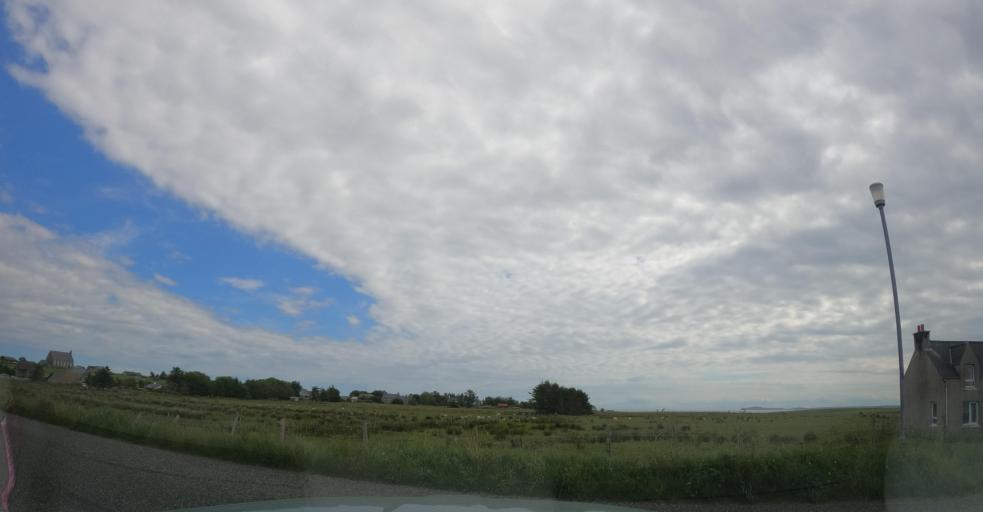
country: GB
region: Scotland
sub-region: Eilean Siar
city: Isle of Lewis
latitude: 58.2725
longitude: -6.2962
